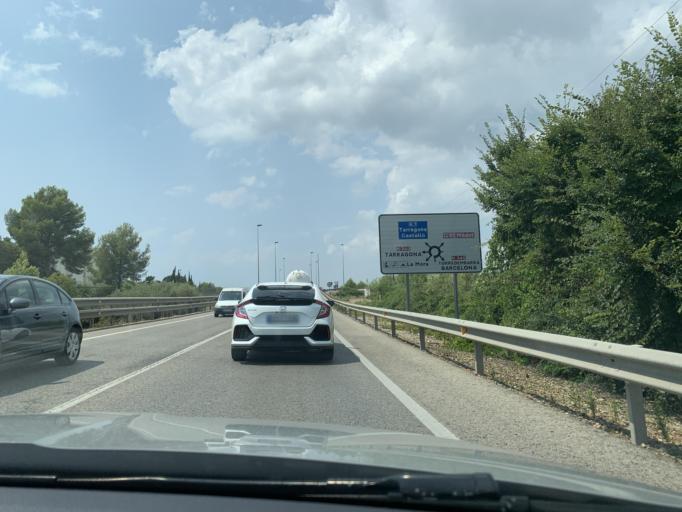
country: ES
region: Catalonia
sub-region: Provincia de Tarragona
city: Altafulla
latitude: 41.1389
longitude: 1.3477
